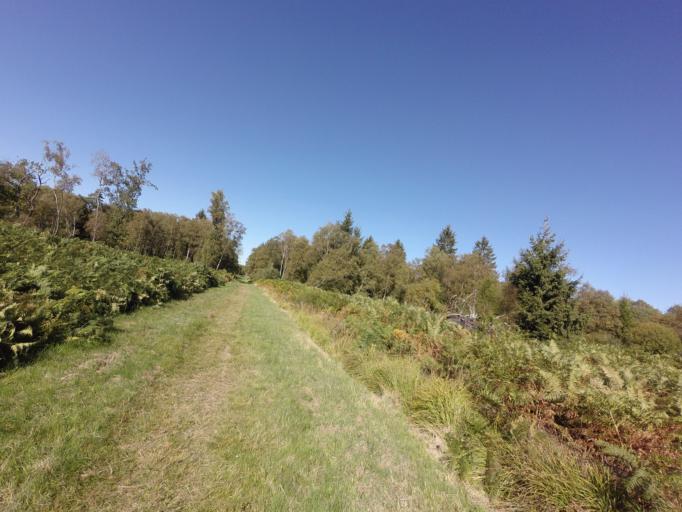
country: DE
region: North Rhine-Westphalia
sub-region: Regierungsbezirk Koln
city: Roetgen
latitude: 50.6018
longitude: 6.1711
